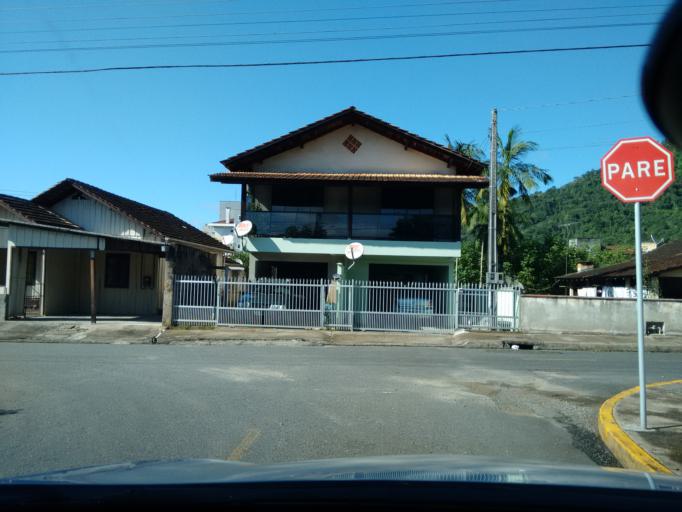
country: BR
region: Santa Catarina
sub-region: Pomerode
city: Pomerode
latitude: -26.7320
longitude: -49.1802
